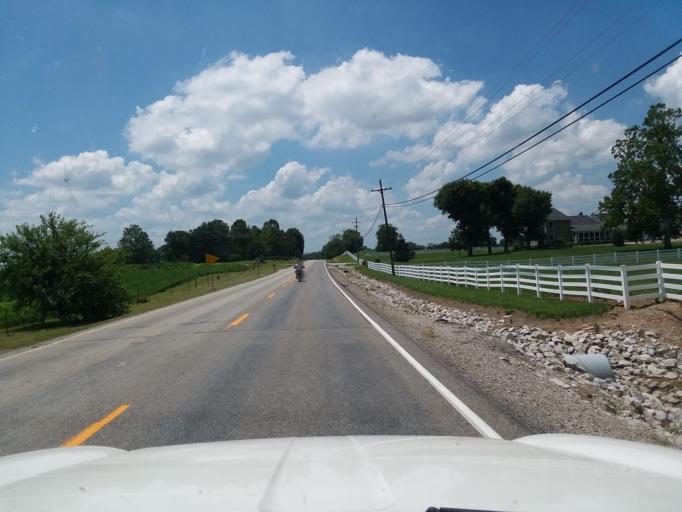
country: US
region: Indiana
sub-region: Johnson County
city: Trafalgar
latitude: 39.3714
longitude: -86.2709
